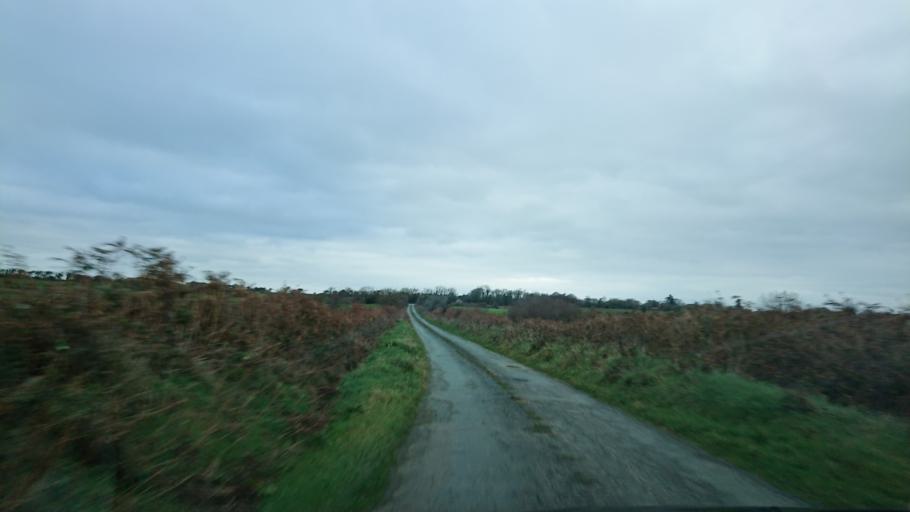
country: IE
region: Munster
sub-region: Waterford
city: Dunmore East
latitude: 52.1856
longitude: -7.0427
